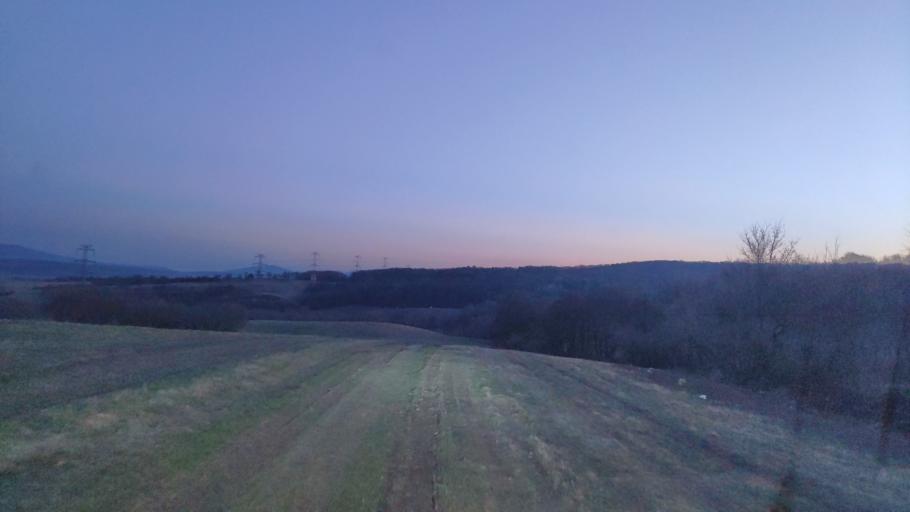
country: SK
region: Kosicky
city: Kosice
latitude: 48.8262
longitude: 21.2642
